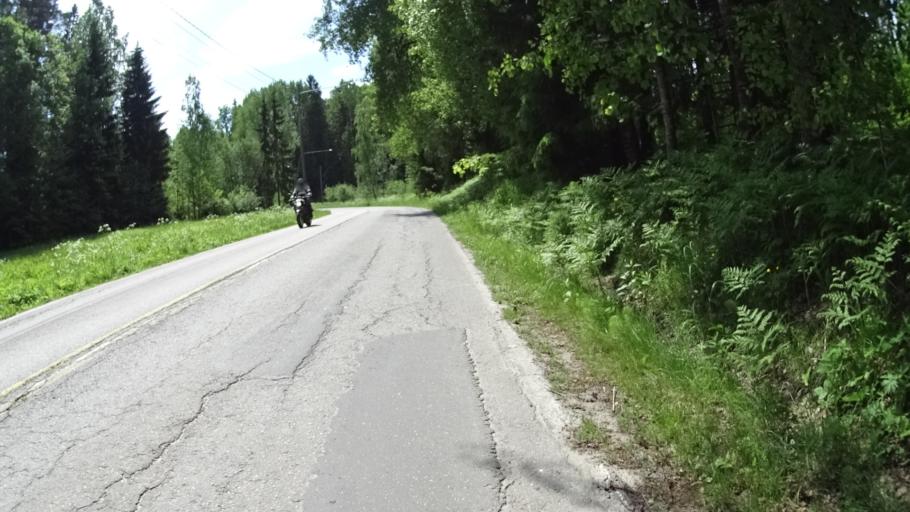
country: FI
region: Uusimaa
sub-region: Helsinki
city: Espoo
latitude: 60.2596
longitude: 24.6524
